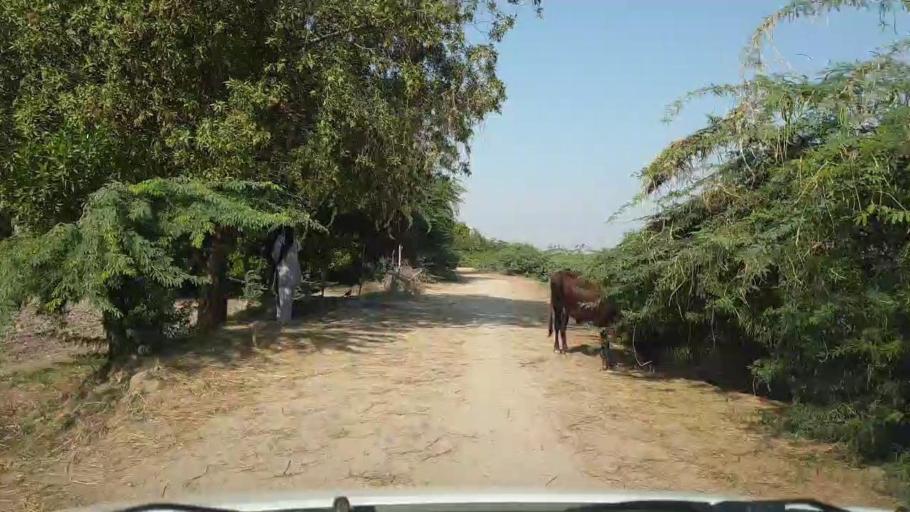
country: PK
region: Sindh
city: Mirpur Sakro
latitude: 24.6007
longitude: 67.6312
